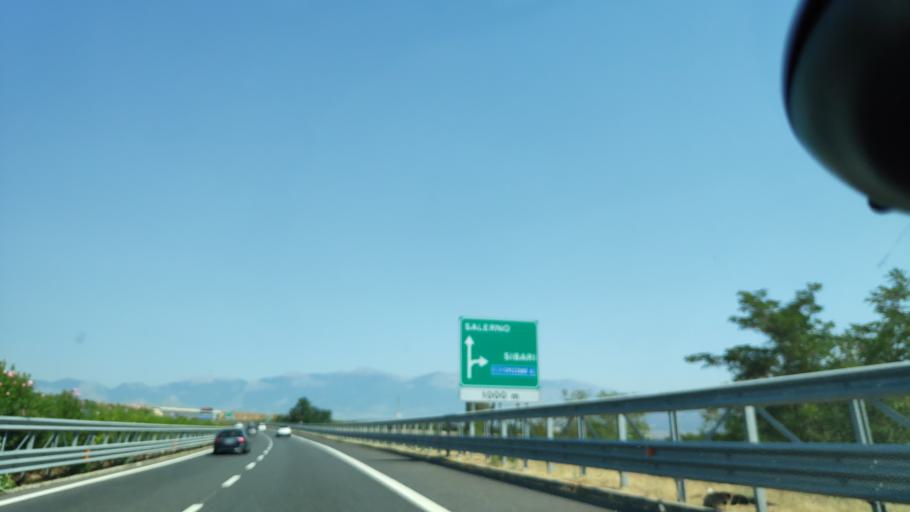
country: IT
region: Calabria
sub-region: Provincia di Cosenza
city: San Lorenzo del Vallo
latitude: 39.7115
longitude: 16.2440
